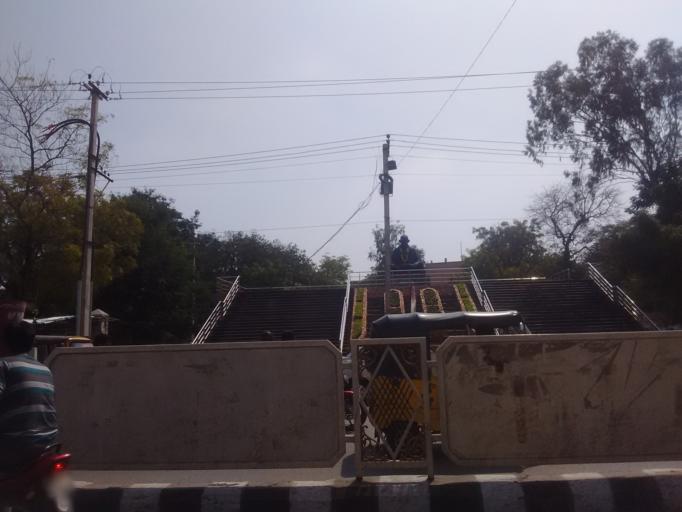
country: IN
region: Telangana
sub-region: Mahbubnagar
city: Alampur
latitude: 15.8293
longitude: 78.0402
